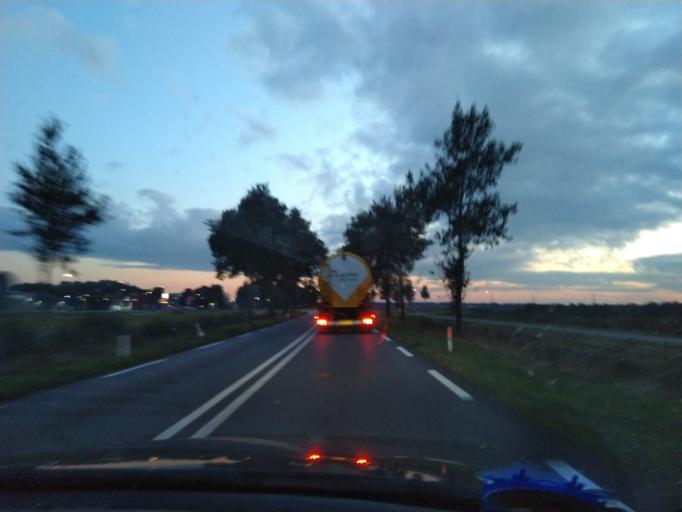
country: NL
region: Groningen
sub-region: Gemeente Pekela
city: Oude Pekela
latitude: 53.0998
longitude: 6.9847
